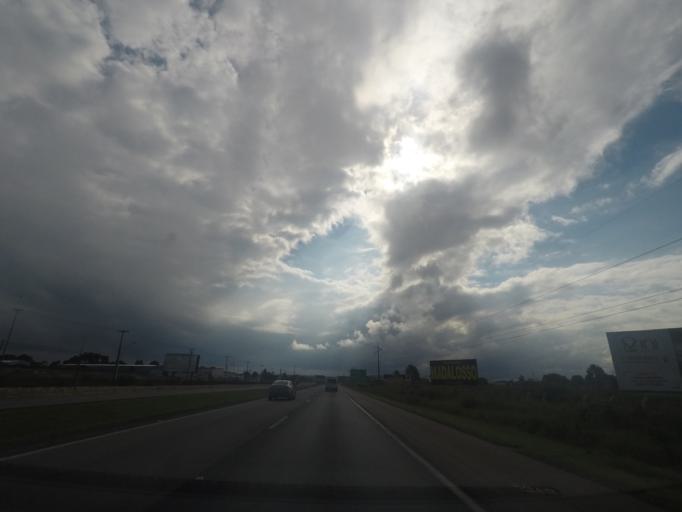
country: BR
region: Parana
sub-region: Piraquara
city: Piraquara
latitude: -25.5167
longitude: -49.1163
